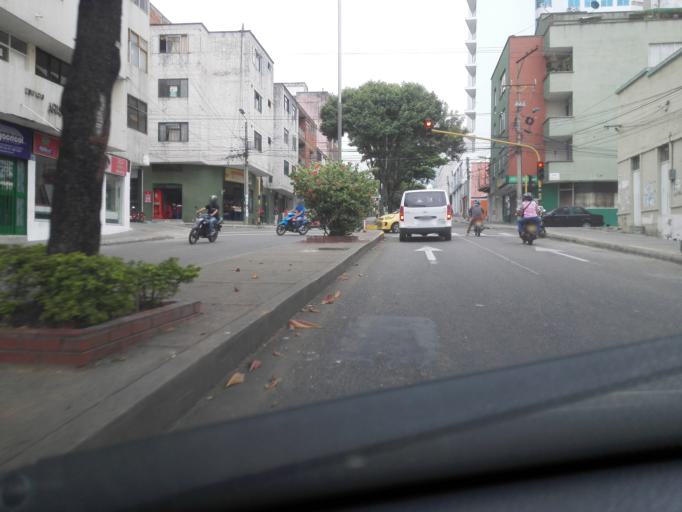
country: CO
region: Santander
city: Bucaramanga
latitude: 7.1206
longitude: -73.1185
